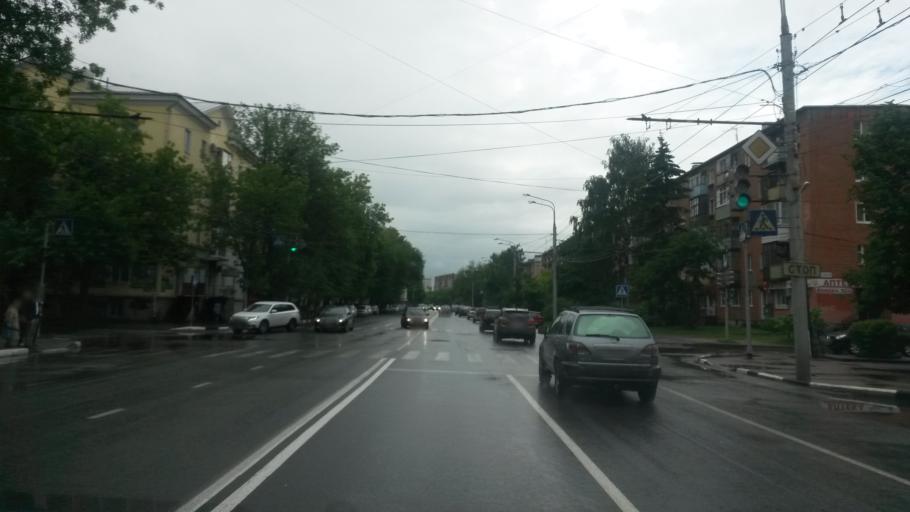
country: RU
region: Jaroslavl
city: Yaroslavl
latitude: 57.6299
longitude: 39.8587
